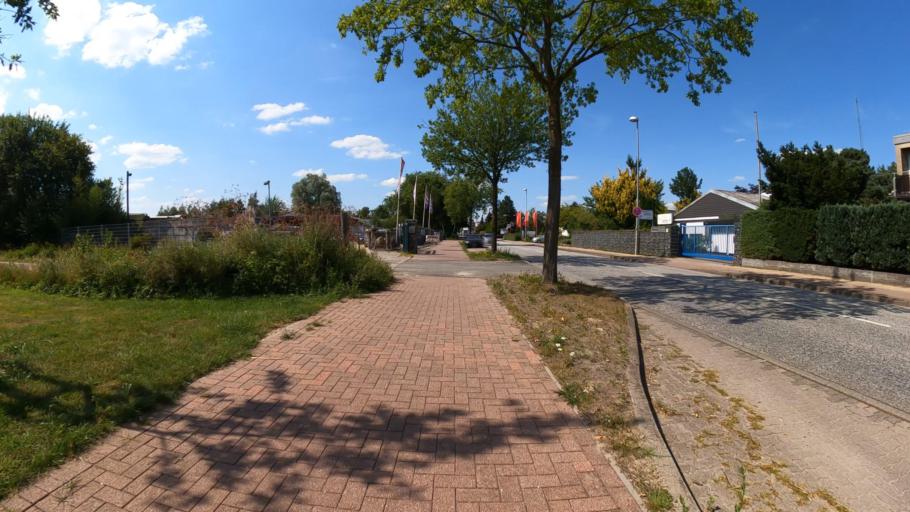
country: DE
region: Schleswig-Holstein
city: Kolln-Reisiek
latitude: 53.7416
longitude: 9.6921
